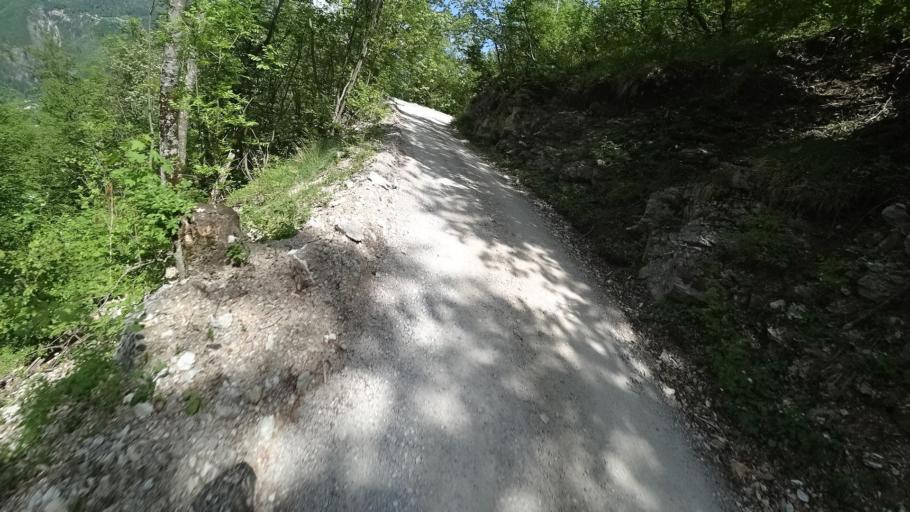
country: BA
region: Federation of Bosnia and Herzegovina
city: Bijela
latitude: 43.5498
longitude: 18.0181
